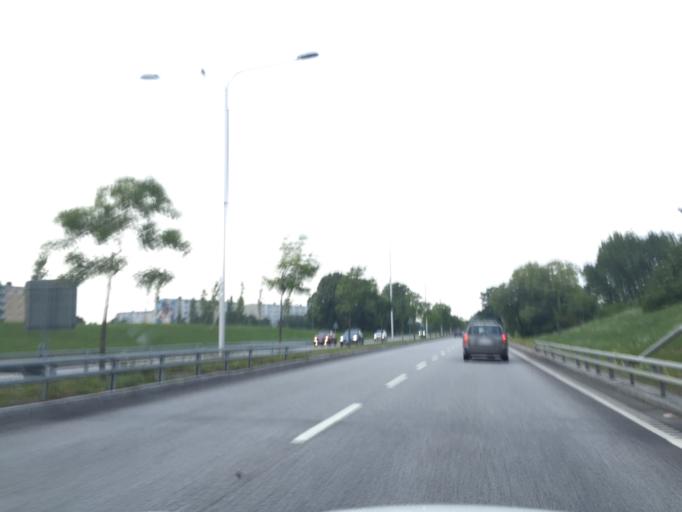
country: SE
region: Skane
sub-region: Malmo
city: Malmoe
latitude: 55.5688
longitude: 12.9872
